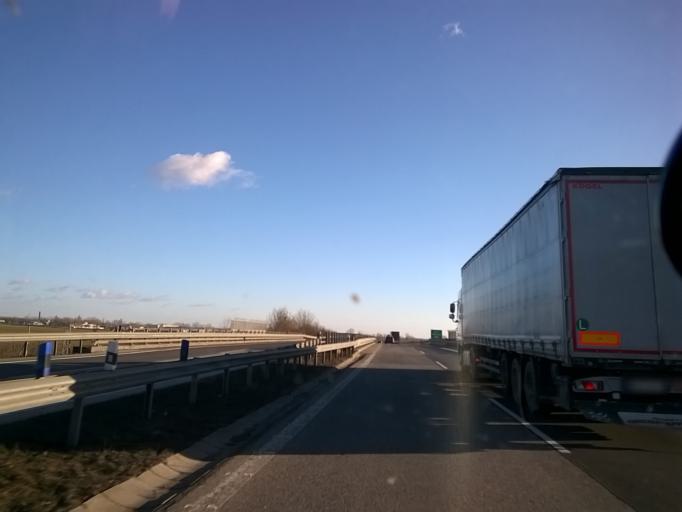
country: SK
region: Trnavsky
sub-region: Okres Galanta
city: Galanta
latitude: 48.2643
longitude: 17.7278
